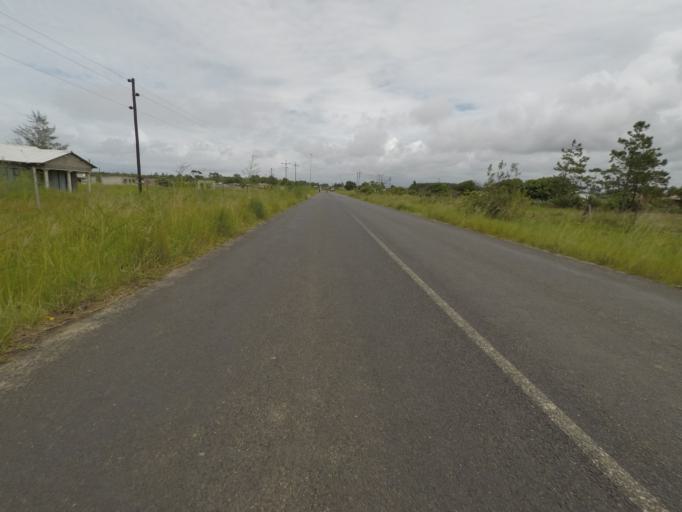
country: ZA
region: KwaZulu-Natal
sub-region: uThungulu District Municipality
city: eSikhawini
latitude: -28.9103
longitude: 31.8684
